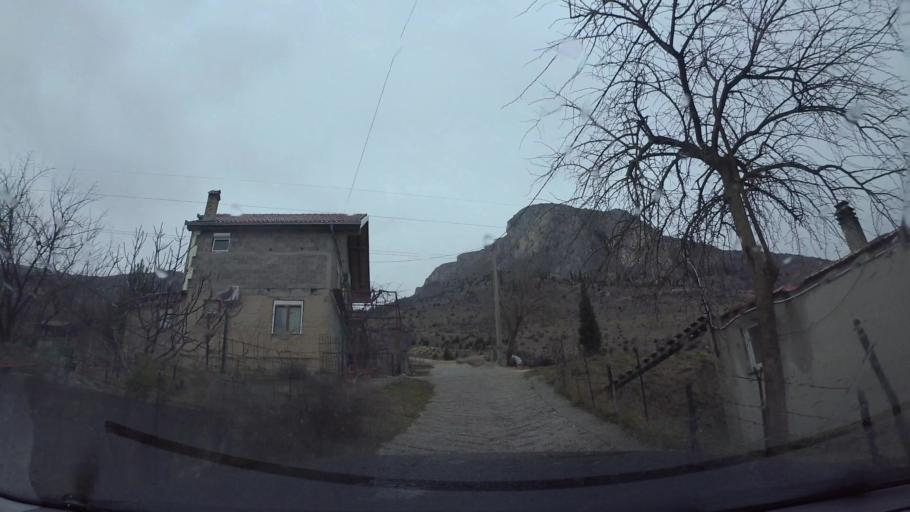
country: BA
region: Federation of Bosnia and Herzegovina
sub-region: Hercegovacko-Bosanski Kanton
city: Mostar
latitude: 43.3455
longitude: 17.8207
